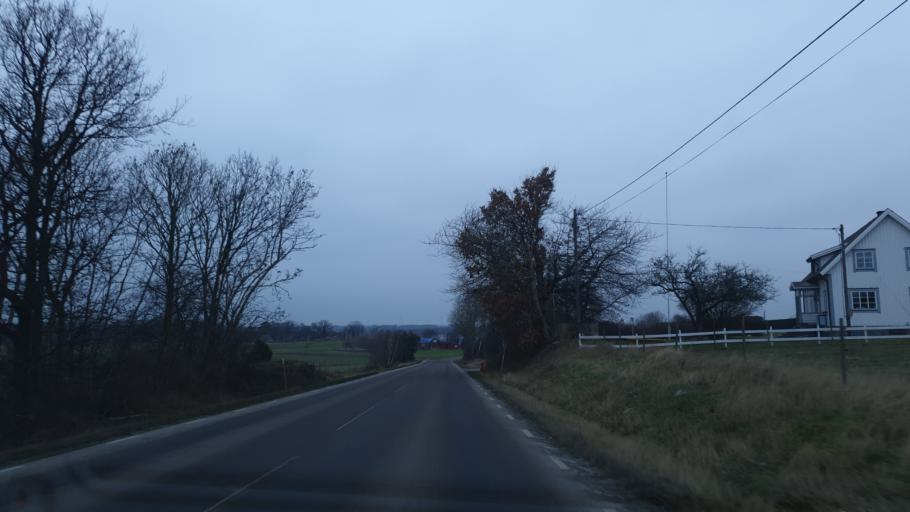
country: SE
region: Blekinge
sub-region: Karlskrona Kommun
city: Sturko
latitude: 56.1335
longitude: 15.7401
